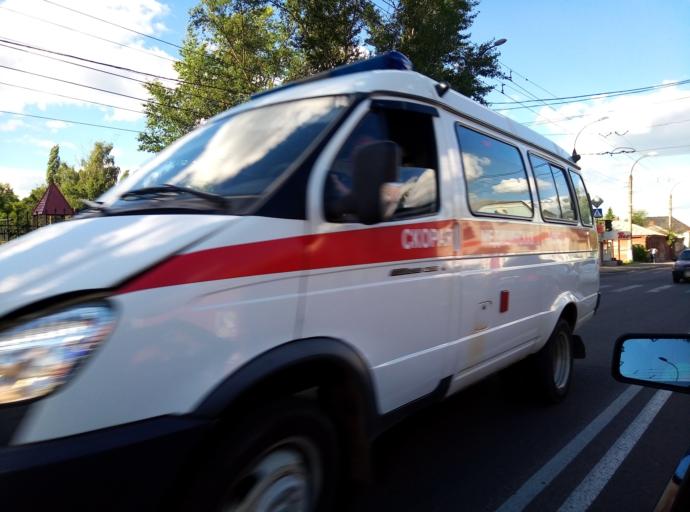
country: RU
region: Kursk
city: Kursk
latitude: 51.7213
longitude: 36.1770
